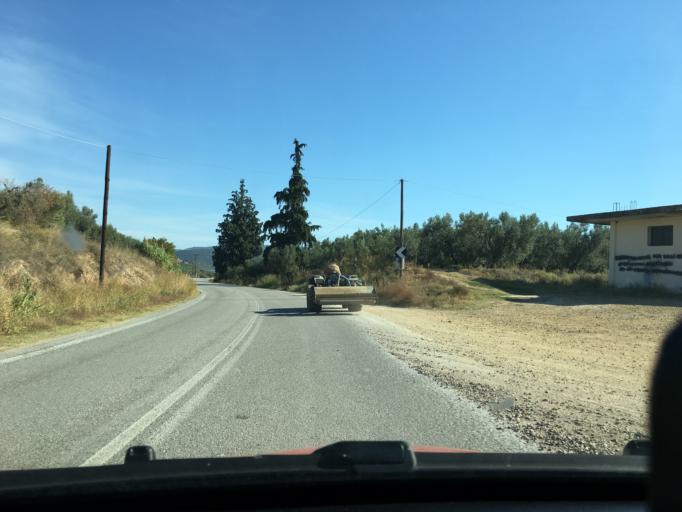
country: GR
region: Central Macedonia
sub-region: Nomos Chalkidikis
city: Ormylia
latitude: 40.2699
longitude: 23.5319
